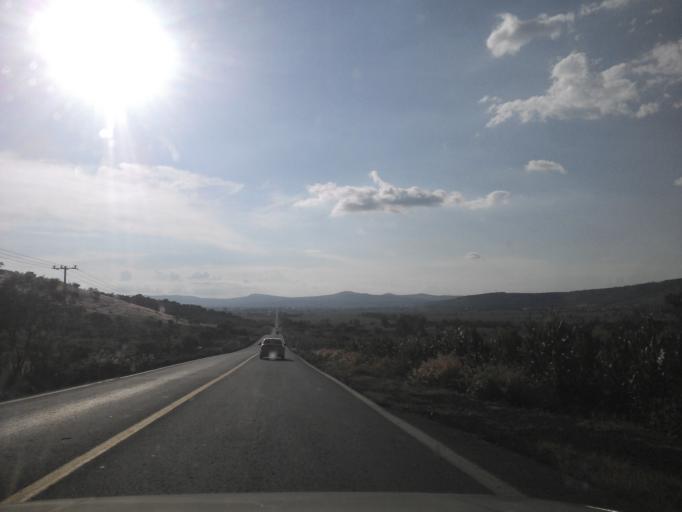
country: MX
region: Jalisco
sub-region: Tototlan
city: Nuevo Refugio de Afuera (Nuevo Refugio)
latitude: 20.5480
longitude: -102.6553
